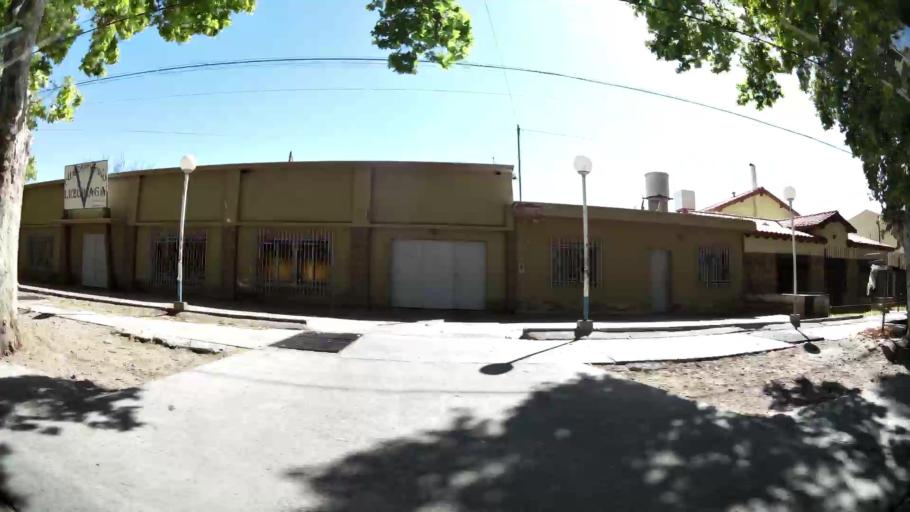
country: AR
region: Mendoza
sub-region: Departamento de Godoy Cruz
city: Godoy Cruz
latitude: -32.9464
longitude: -68.8043
